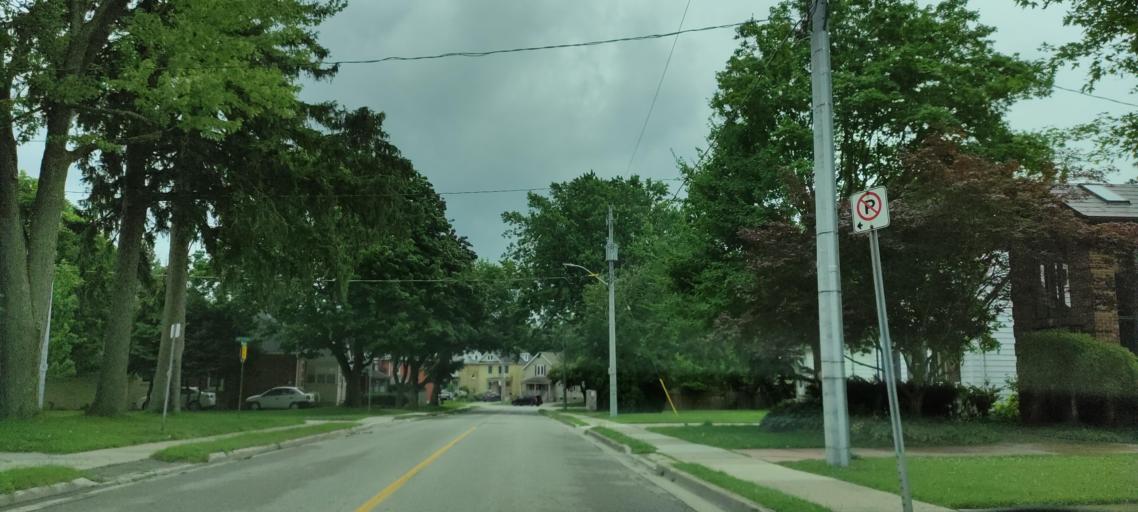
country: CA
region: Ontario
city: Stratford
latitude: 43.3781
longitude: -80.9799
